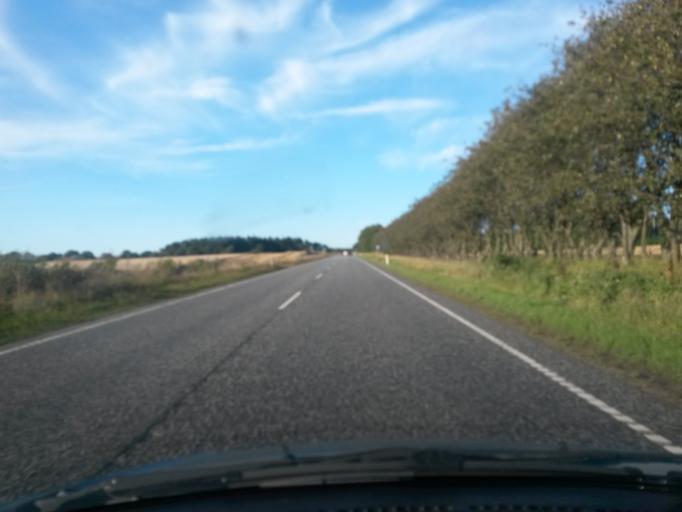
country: DK
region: Central Jutland
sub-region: Silkeborg Kommune
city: Kjellerup
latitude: 56.3133
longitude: 9.3282
